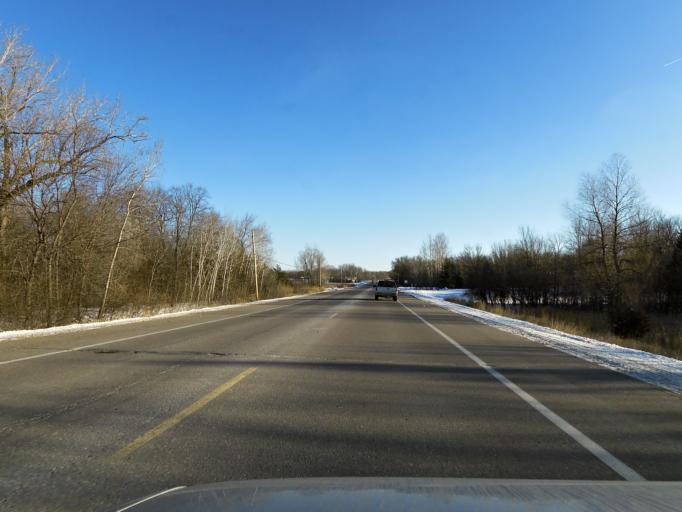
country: US
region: Minnesota
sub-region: Scott County
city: Shakopee
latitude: 44.7316
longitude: -93.4954
